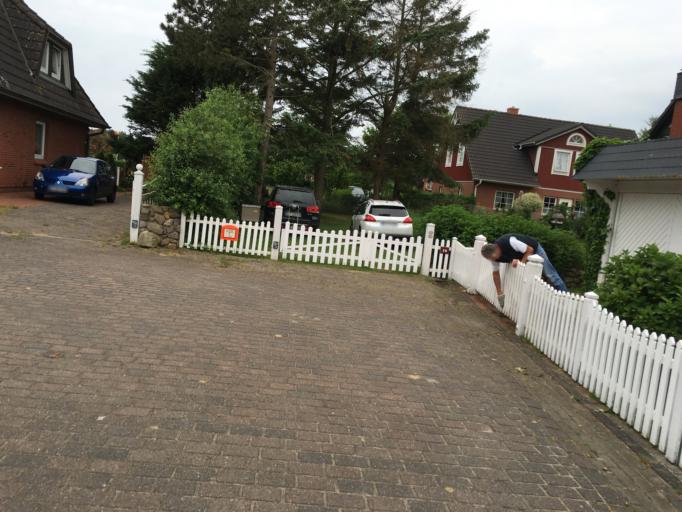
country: DE
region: Schleswig-Holstein
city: Norddorf
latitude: 54.6779
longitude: 8.3363
